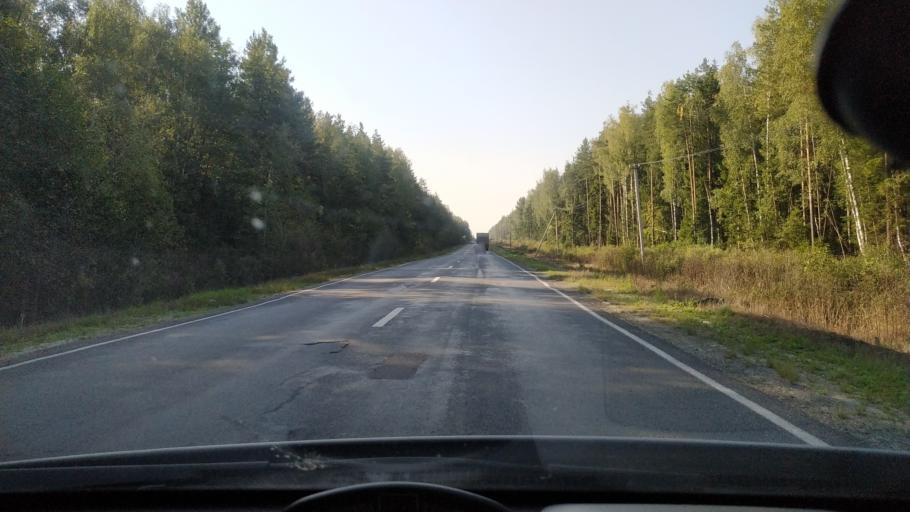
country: RU
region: Moskovskaya
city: Tugolesskiy Bor
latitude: 55.5141
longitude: 39.7119
